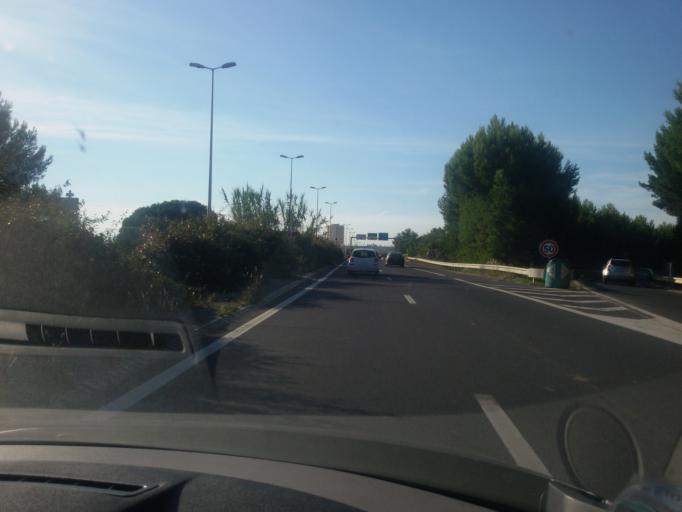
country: FR
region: Languedoc-Roussillon
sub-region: Departement de l'Herault
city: Lattes
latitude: 43.5862
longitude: 3.8950
